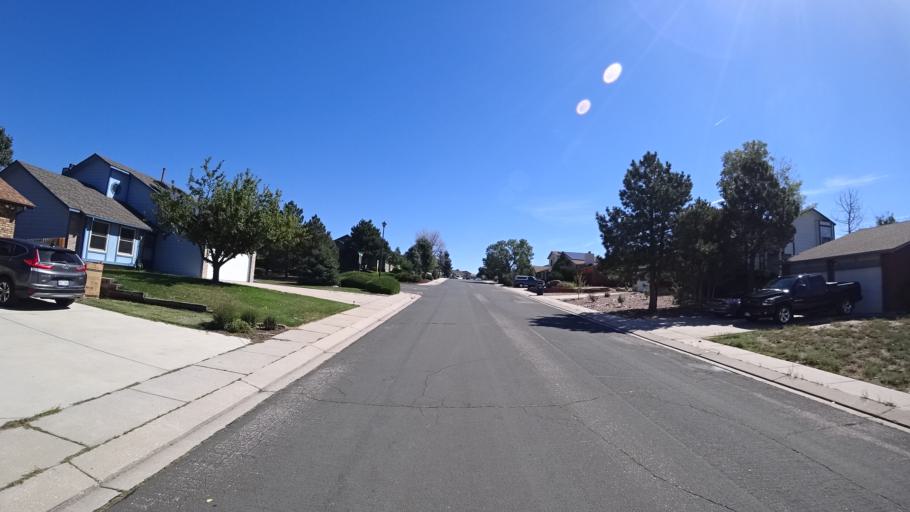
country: US
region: Colorado
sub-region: El Paso County
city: Black Forest
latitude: 38.9466
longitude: -104.7497
